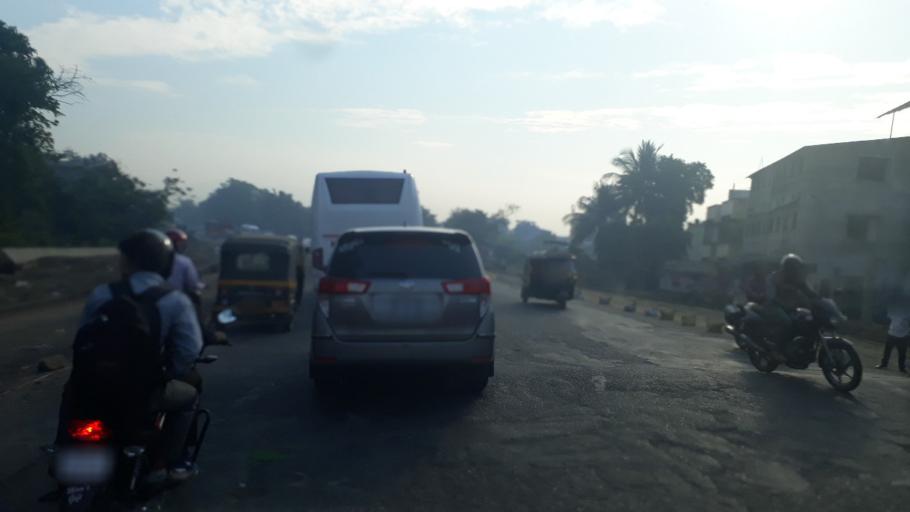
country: IN
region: Maharashtra
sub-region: Raigarh
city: Kalundri
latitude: 18.9748
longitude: 73.1191
